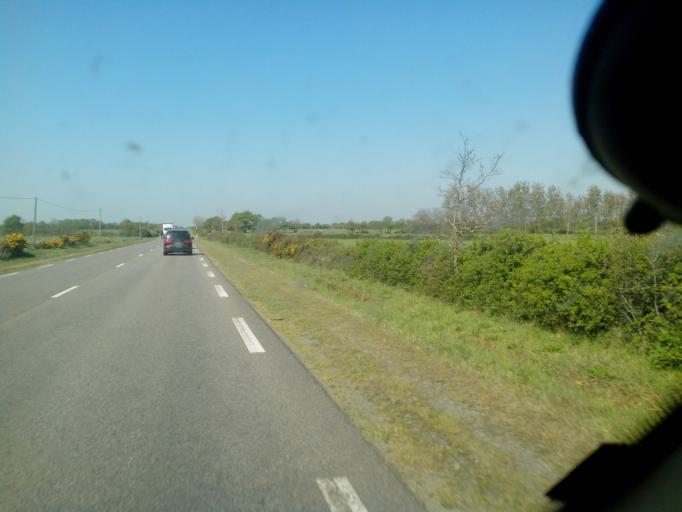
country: FR
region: Pays de la Loire
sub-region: Departement de la Loire-Atlantique
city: Chauve
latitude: 47.1115
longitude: -1.9934
